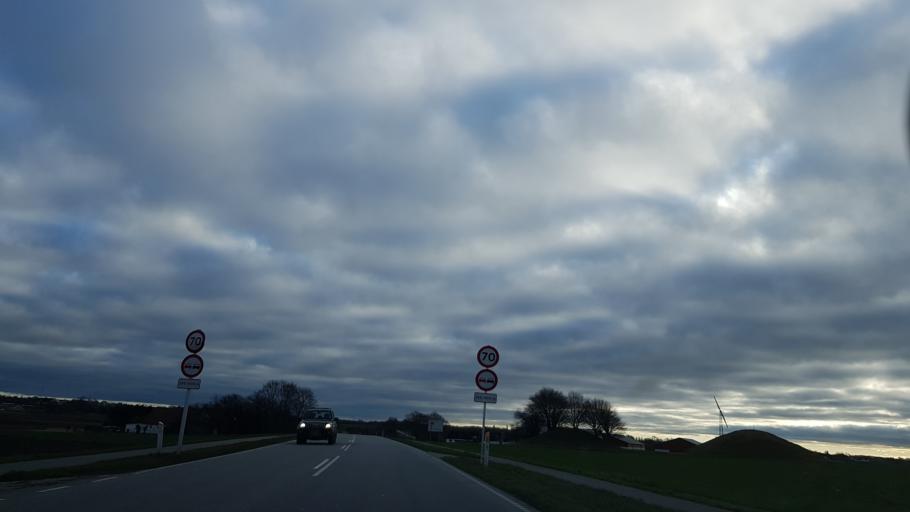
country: DK
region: Zealand
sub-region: Kalundborg Kommune
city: Hong
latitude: 55.5074
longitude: 11.2589
